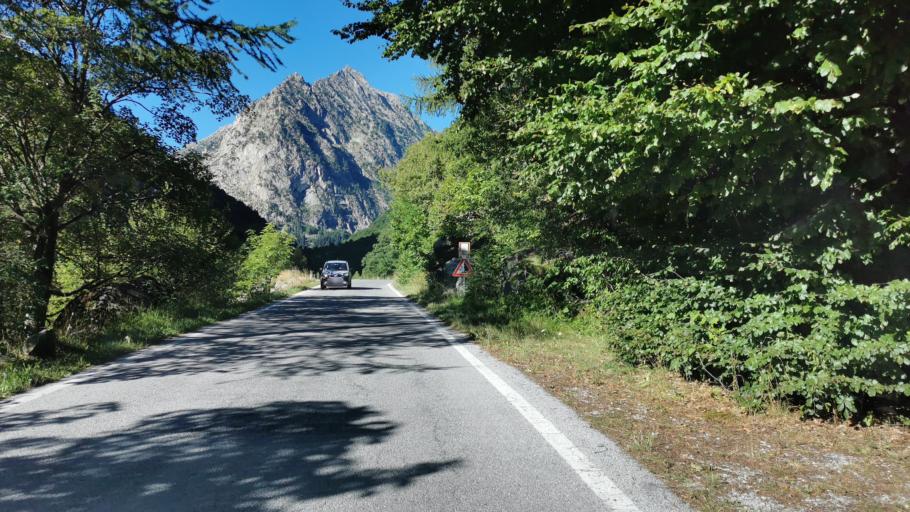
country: IT
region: Piedmont
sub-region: Provincia di Cuneo
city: Demonte
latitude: 44.2188
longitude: 7.2848
